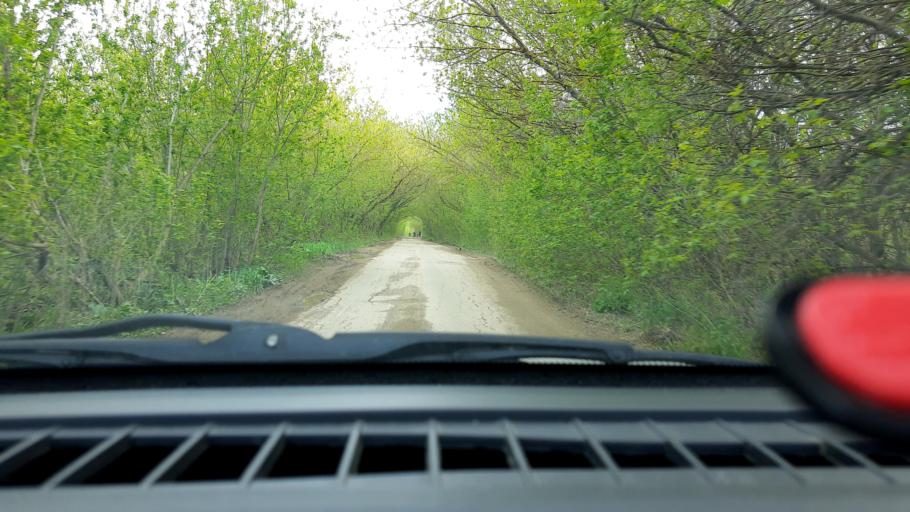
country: RU
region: Nizjnij Novgorod
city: Neklyudovo
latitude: 56.3897
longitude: 43.8423
